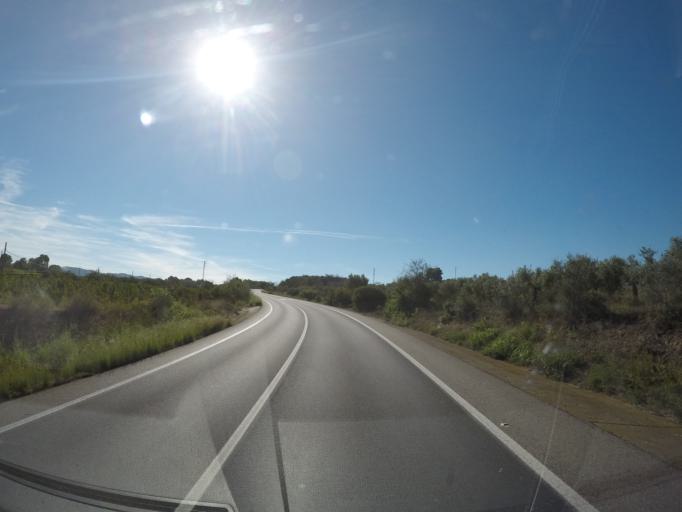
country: ES
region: Catalonia
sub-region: Provincia de Tarragona
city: Rasquera
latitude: 41.0179
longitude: 0.6088
